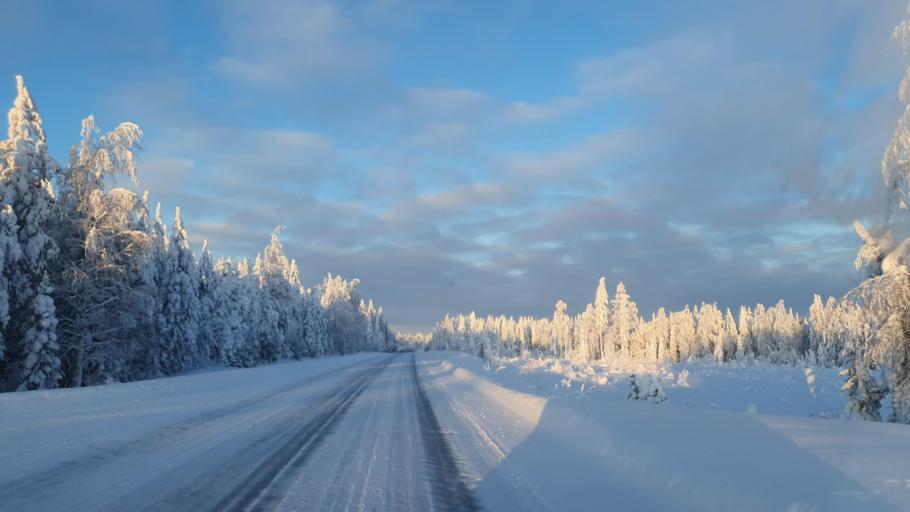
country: FI
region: Kainuu
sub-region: Kajaani
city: Vuokatti
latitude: 64.2439
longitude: 28.2315
